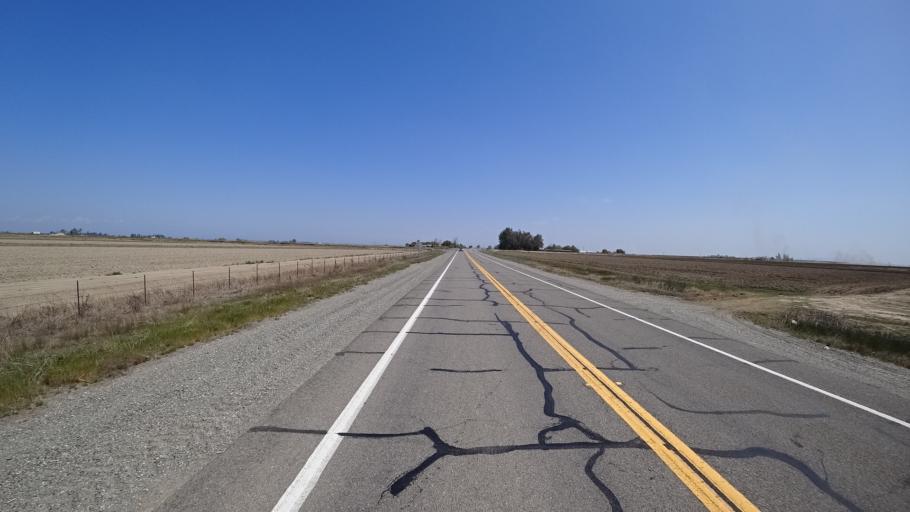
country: US
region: California
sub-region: Glenn County
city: Willows
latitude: 39.5239
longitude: -122.1240
